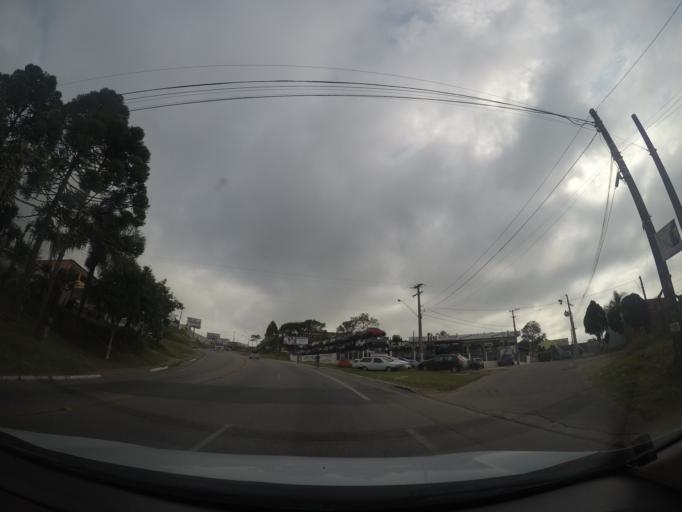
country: BR
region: Parana
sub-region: Colombo
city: Colombo
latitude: -25.3606
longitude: -49.2190
